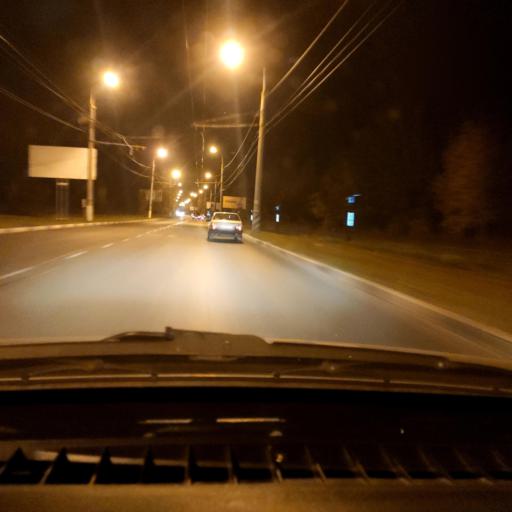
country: RU
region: Samara
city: Tol'yatti
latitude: 53.4960
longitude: 49.3873
